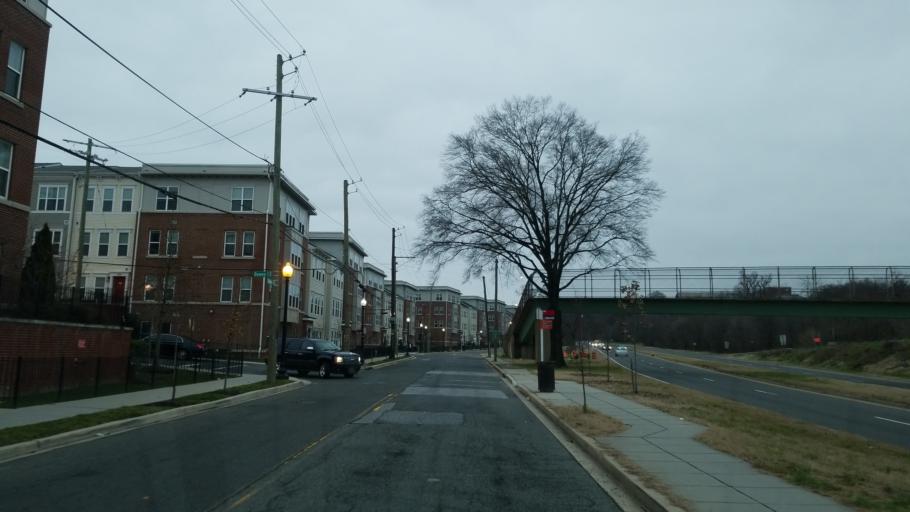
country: US
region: Maryland
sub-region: Prince George's County
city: Glassmanor
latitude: 38.8593
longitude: -76.9935
